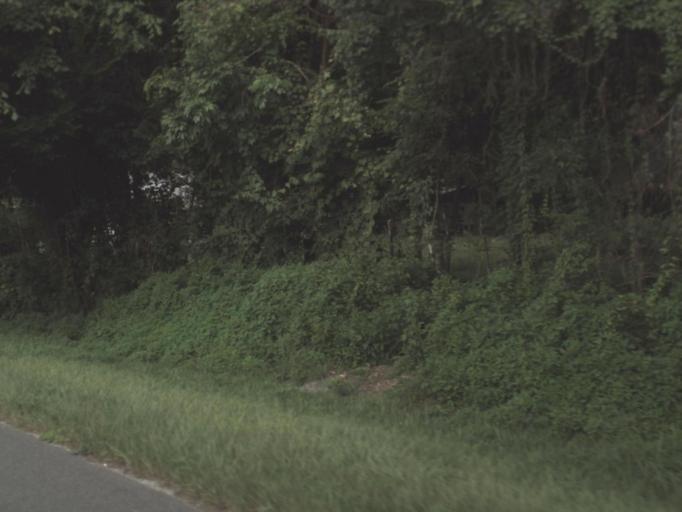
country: US
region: Florida
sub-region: Hernando County
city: Ridge Manor
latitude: 28.5227
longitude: -82.1668
